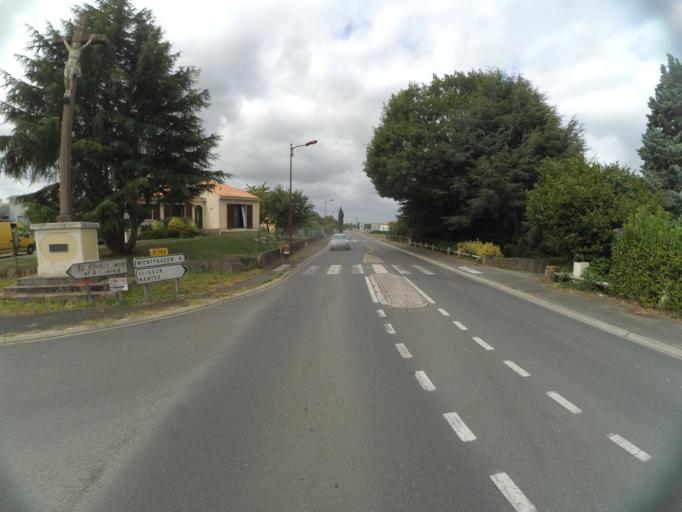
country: FR
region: Pays de la Loire
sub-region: Departement de Maine-et-Loire
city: Villedieu-la-Blouere
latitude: 47.1427
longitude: -1.0692
